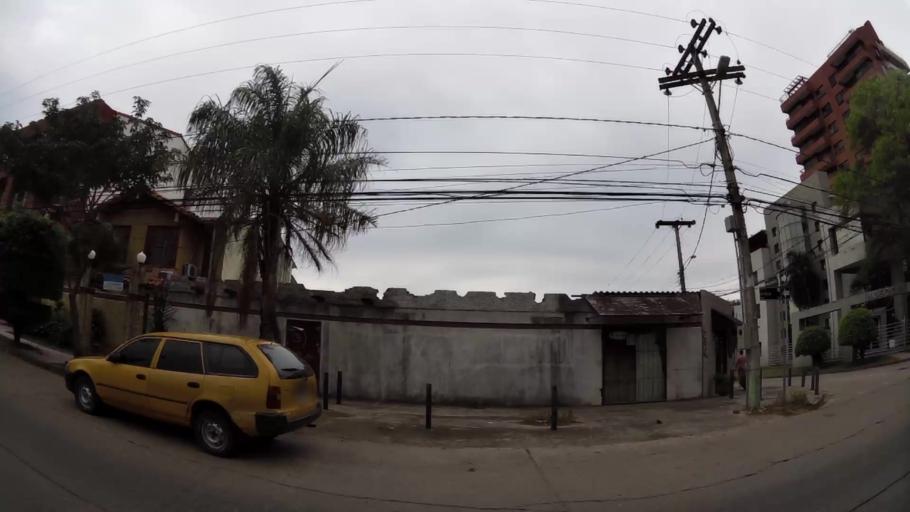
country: BO
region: Santa Cruz
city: Santa Cruz de la Sierra
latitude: -17.7644
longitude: -63.1910
